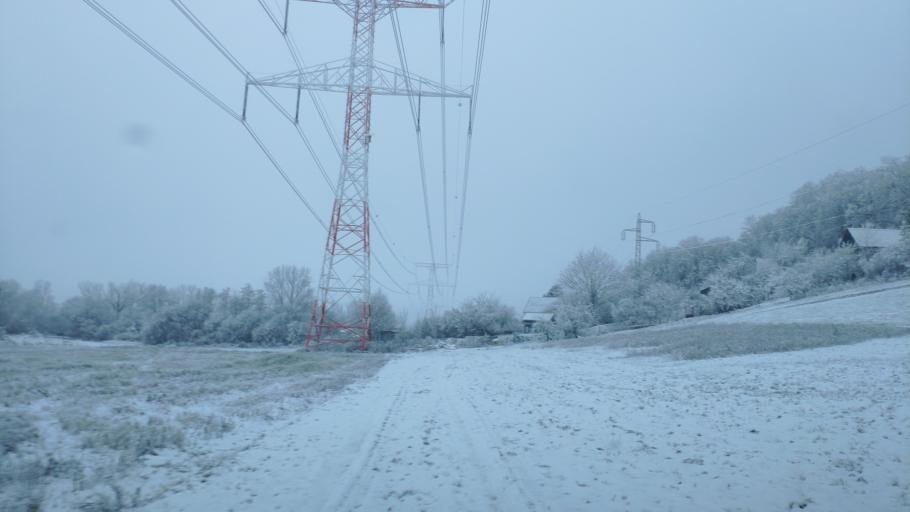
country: SK
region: Kosicky
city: Kosice
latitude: 48.6481
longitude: 21.1702
